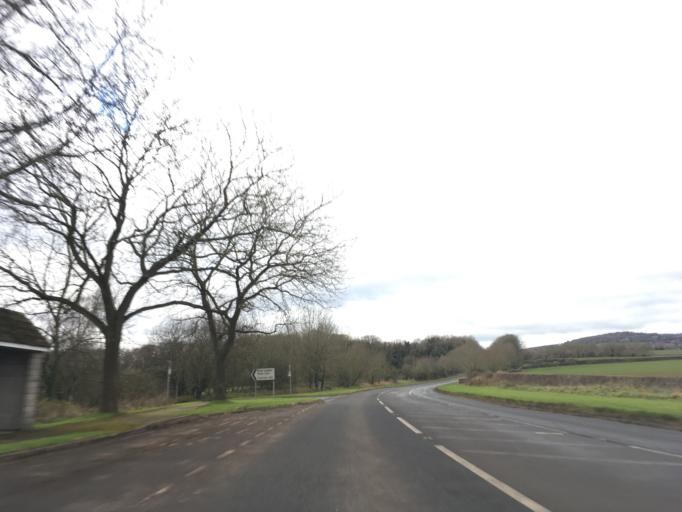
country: GB
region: Wales
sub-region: Newport
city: Llanvaches
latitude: 51.6136
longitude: -2.7977
